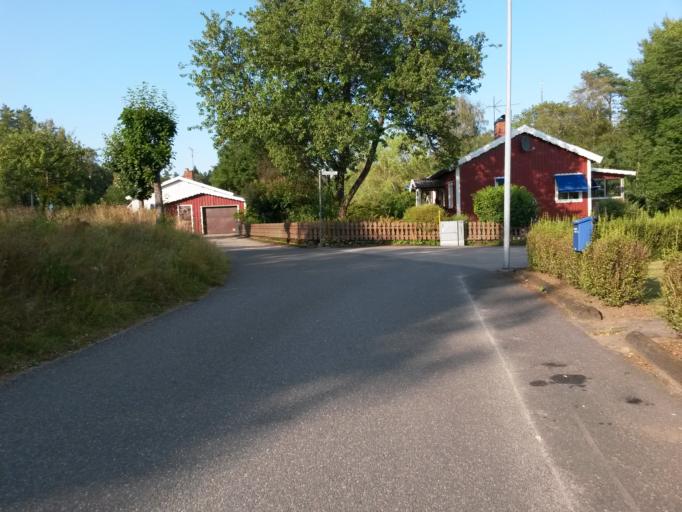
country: SE
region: Vaestra Goetaland
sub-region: Vargarda Kommun
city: Vargarda
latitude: 58.0341
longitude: 12.8238
